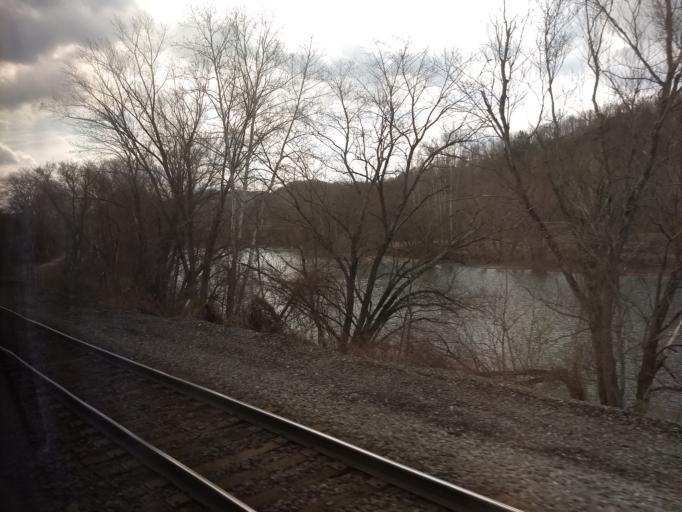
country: US
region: Pennsylvania
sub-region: Huntingdon County
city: Huntingdon
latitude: 40.4816
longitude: -78.0057
